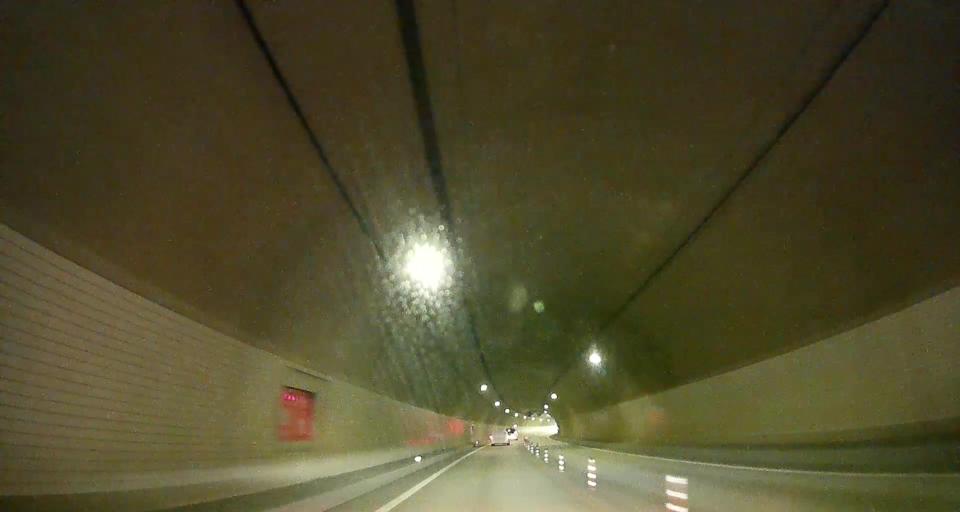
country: JP
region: Iwate
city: Miyako
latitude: 39.9323
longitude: 141.8508
